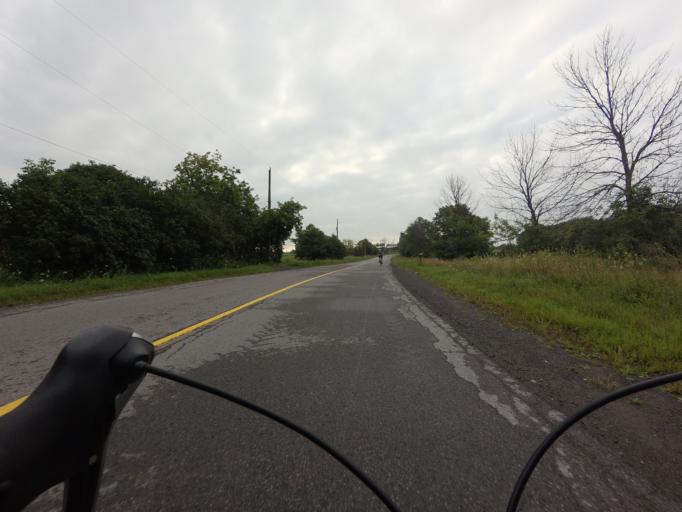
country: CA
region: Ontario
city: Bells Corners
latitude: 45.2633
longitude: -75.8127
